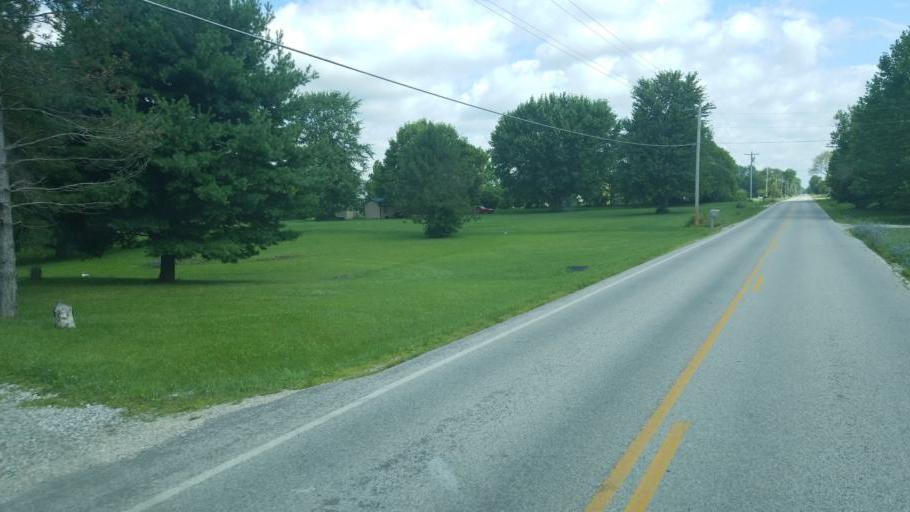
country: US
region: Ohio
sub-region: Delaware County
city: Sunbury
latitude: 40.2937
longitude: -82.9348
